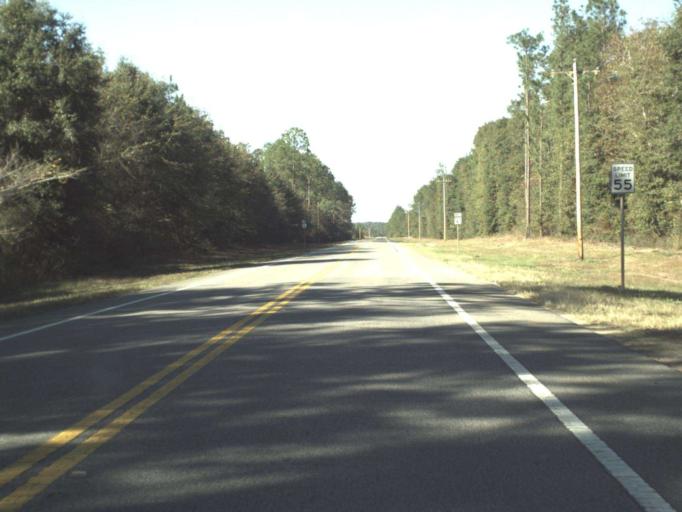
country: US
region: Florida
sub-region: Okaloosa County
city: Crestview
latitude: 30.8208
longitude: -86.7195
